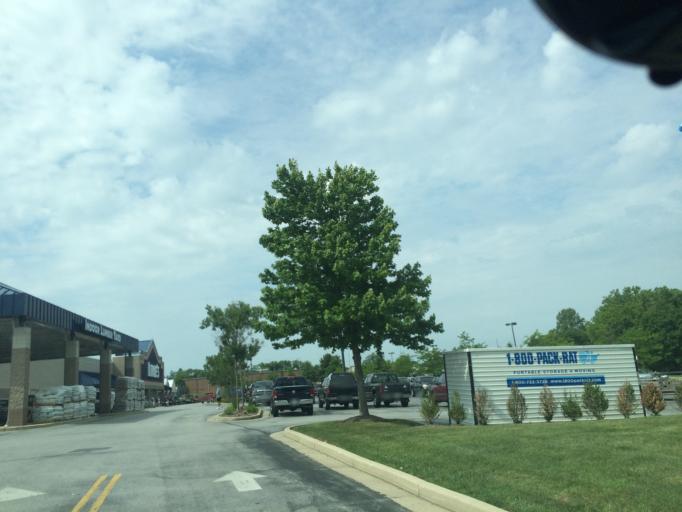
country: US
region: Maryland
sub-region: Carroll County
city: Westminster
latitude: 39.5666
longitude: -76.9699
